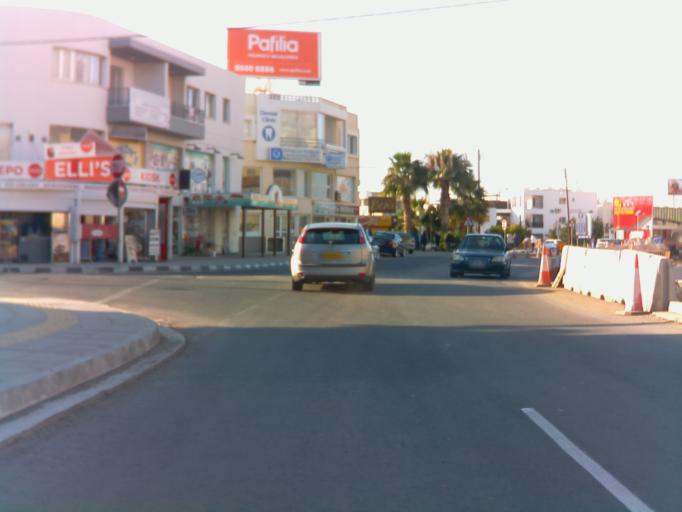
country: CY
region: Pafos
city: Paphos
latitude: 34.7647
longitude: 32.4120
